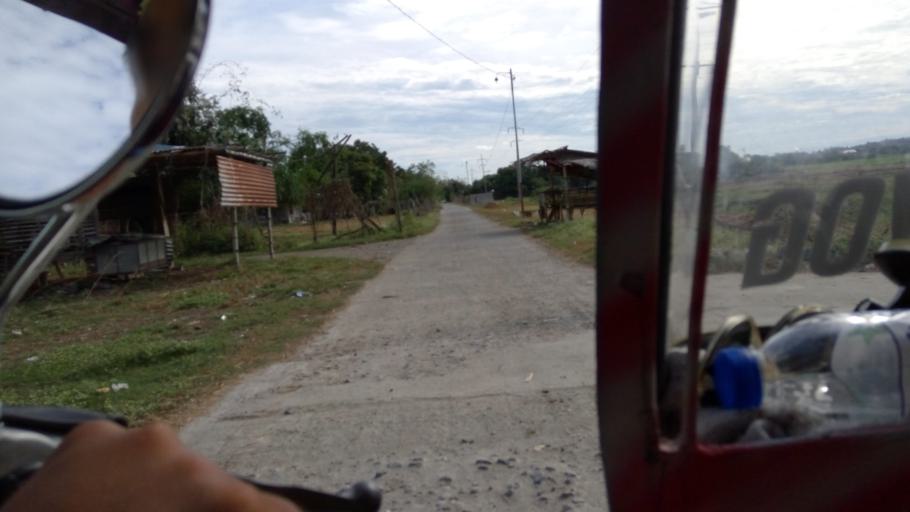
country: PH
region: Ilocos
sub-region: Province of La Union
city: San Eugenio
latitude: 16.3735
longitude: 120.3523
